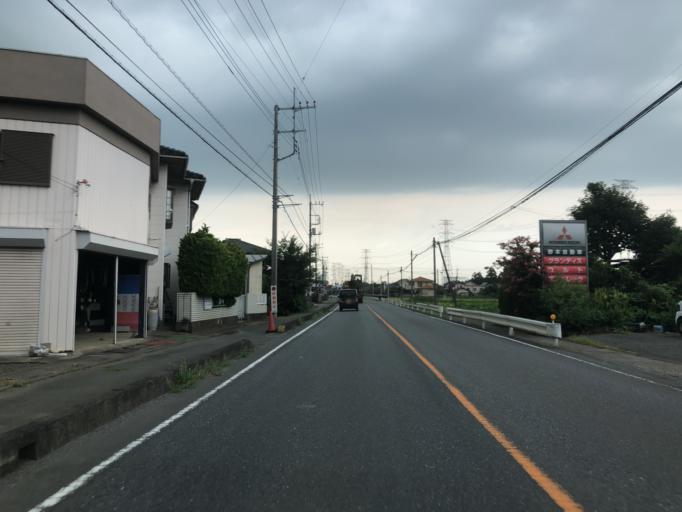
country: JP
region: Saitama
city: Sakado
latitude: 36.0214
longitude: 139.3978
